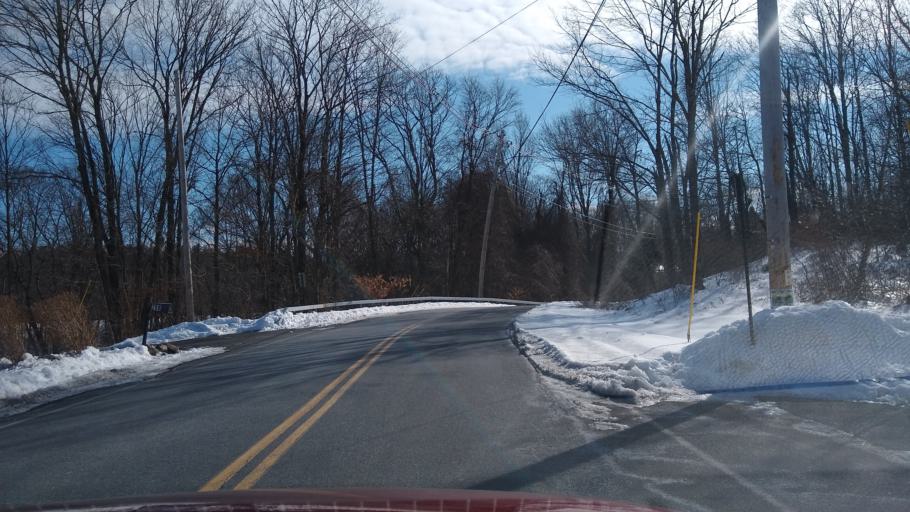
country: US
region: New York
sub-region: Ulster County
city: Kingston
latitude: 41.9224
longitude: -74.0111
